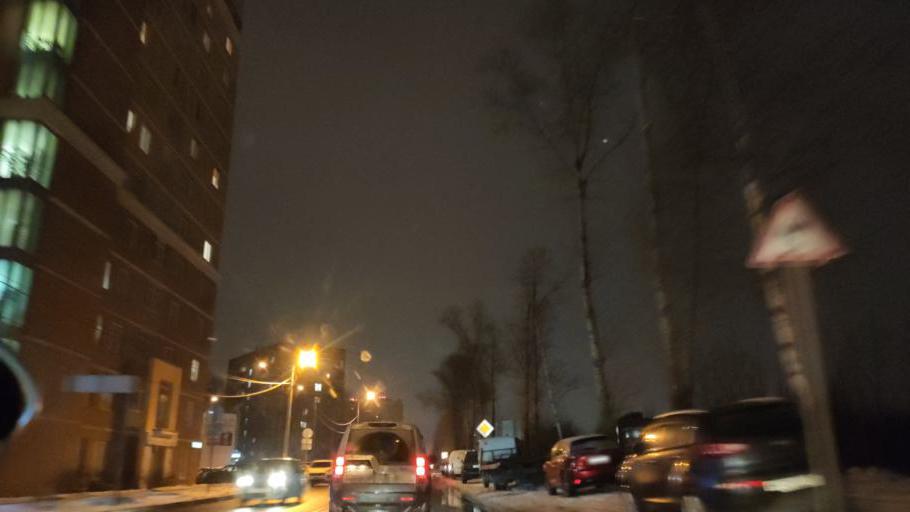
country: RU
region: Moskovskaya
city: Odintsovo
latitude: 55.6867
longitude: 37.2586
